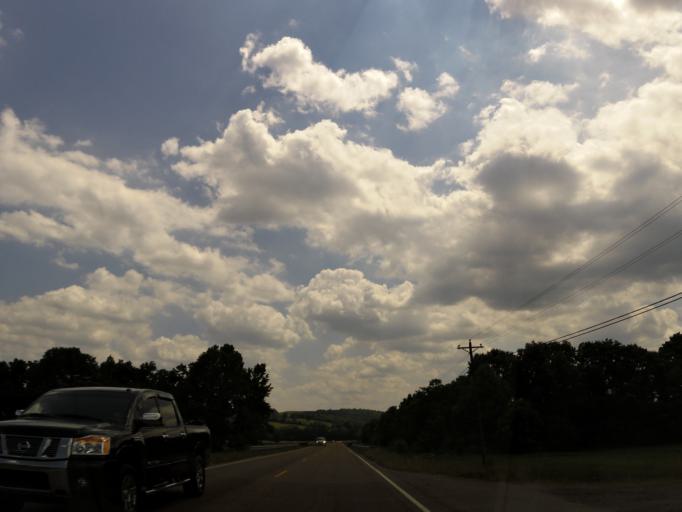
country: US
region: Tennessee
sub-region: Bledsoe County
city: Pikeville
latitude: 35.5469
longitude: -85.2552
